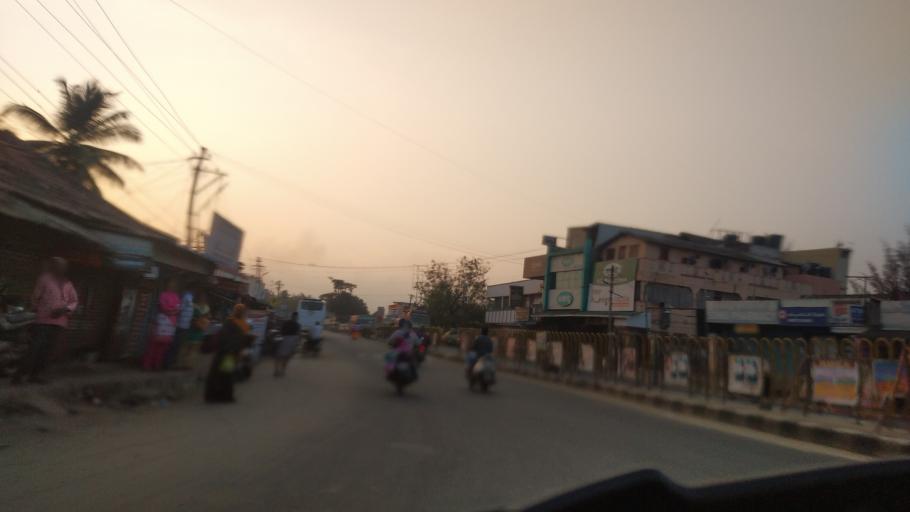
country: IN
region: Tamil Nadu
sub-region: Coimbatore
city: Coimbatore
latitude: 10.9746
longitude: 76.9620
